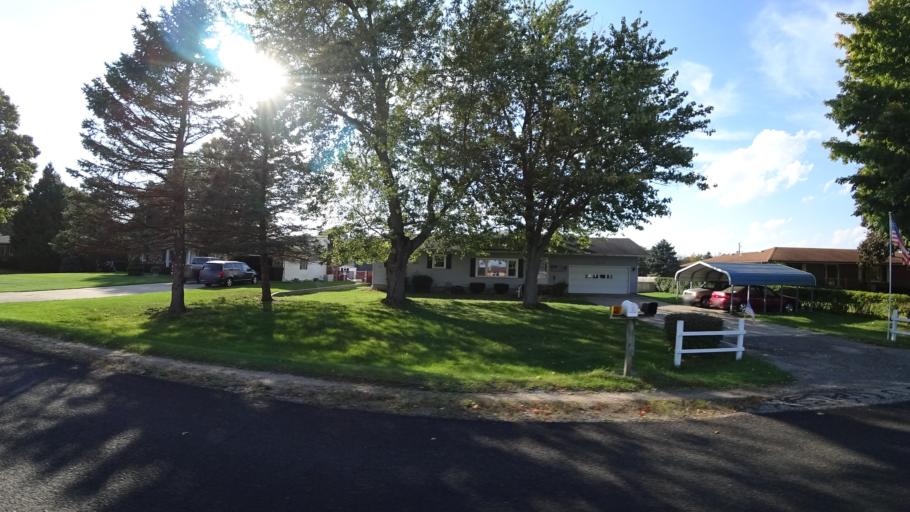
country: US
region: Michigan
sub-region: Saint Joseph County
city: Three Rivers
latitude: 41.9501
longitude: -85.6515
